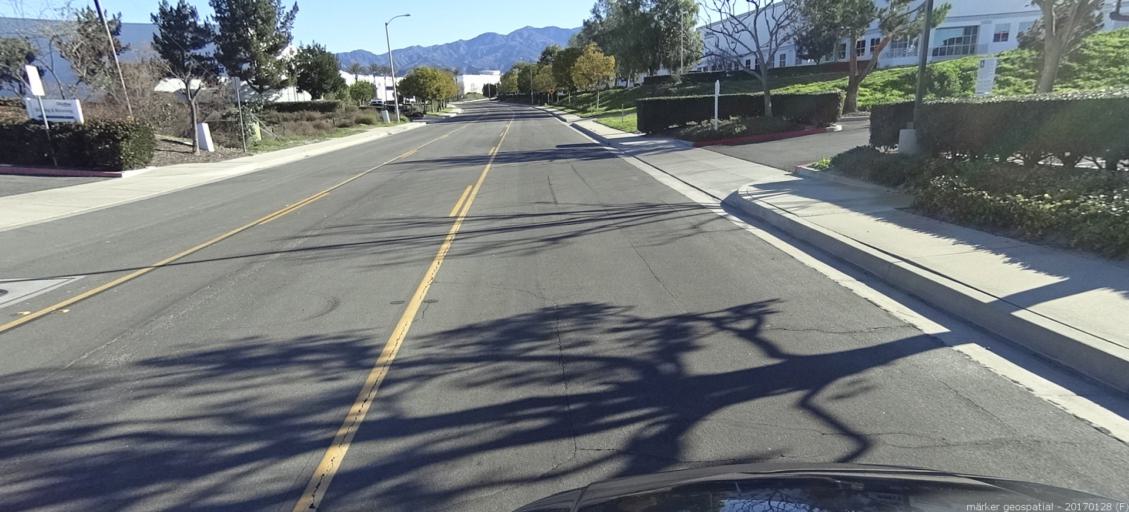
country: US
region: California
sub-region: Orange County
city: Lake Forest
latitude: 33.6663
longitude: -117.6910
